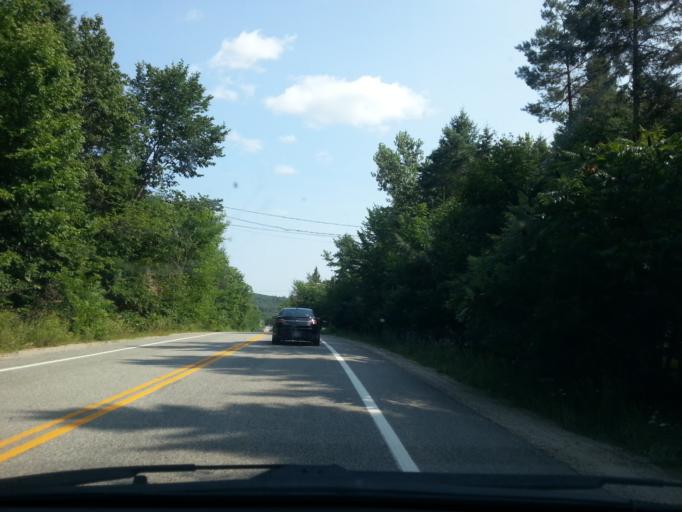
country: CA
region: Quebec
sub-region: Outaouais
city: Wakefield
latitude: 45.5770
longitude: -75.8751
